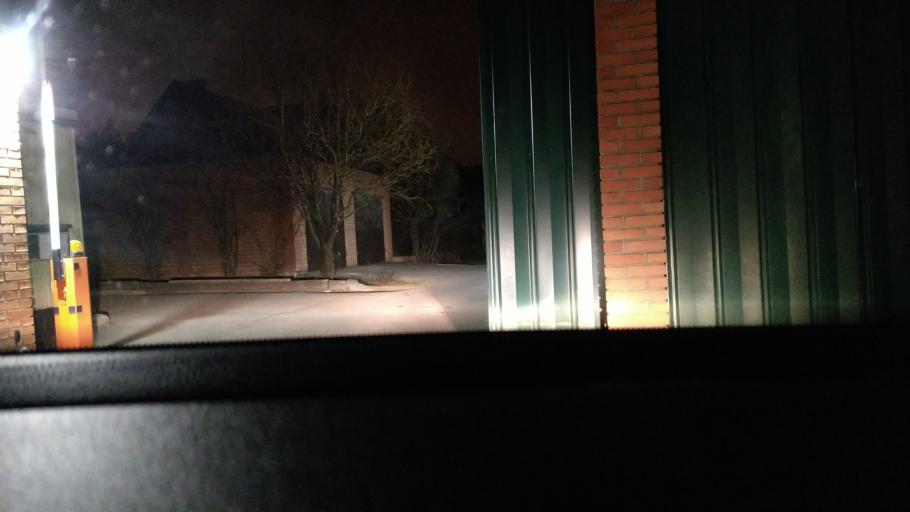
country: RU
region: Moskovskaya
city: Petrovo-Dal'neye
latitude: 55.7212
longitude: 37.2035
